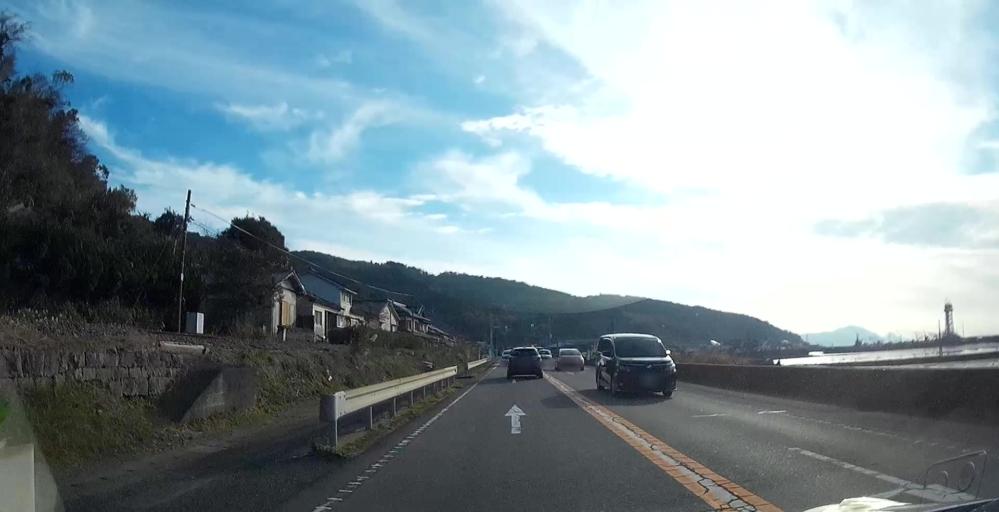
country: JP
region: Kumamoto
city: Uto
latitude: 32.6968
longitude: 130.5664
